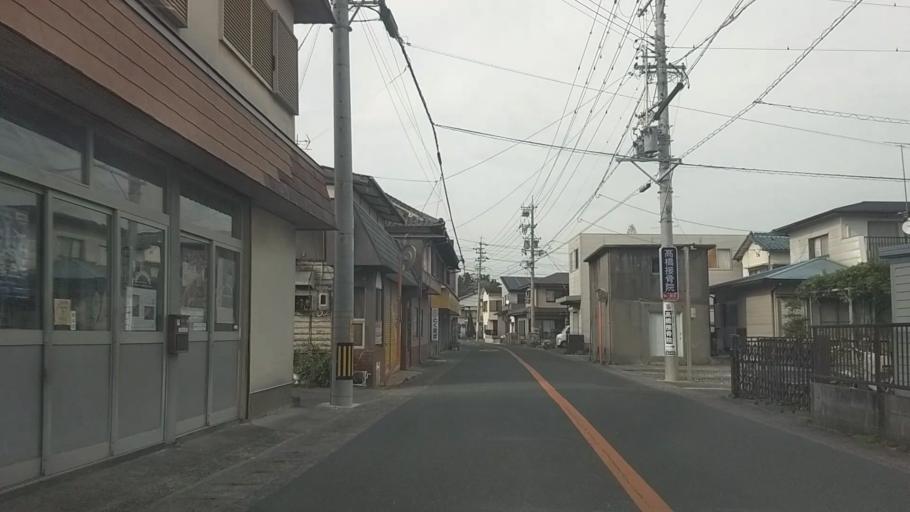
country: JP
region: Shizuoka
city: Kosai-shi
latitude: 34.7615
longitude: 137.6126
